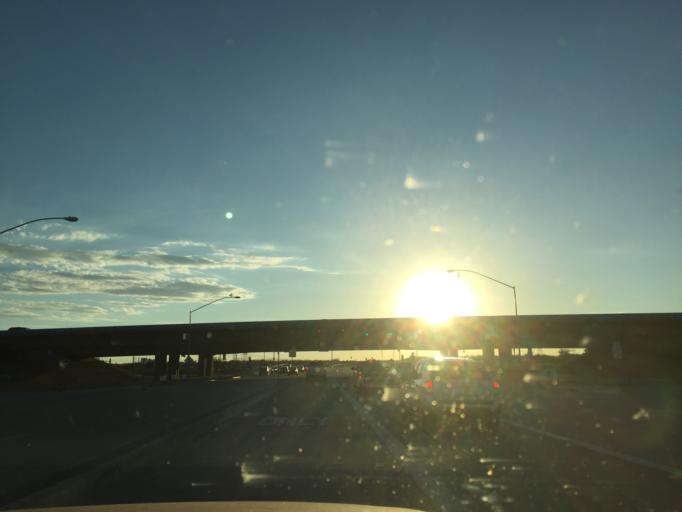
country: US
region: Arizona
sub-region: Maricopa County
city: Sun City West
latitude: 33.7137
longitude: -112.3096
